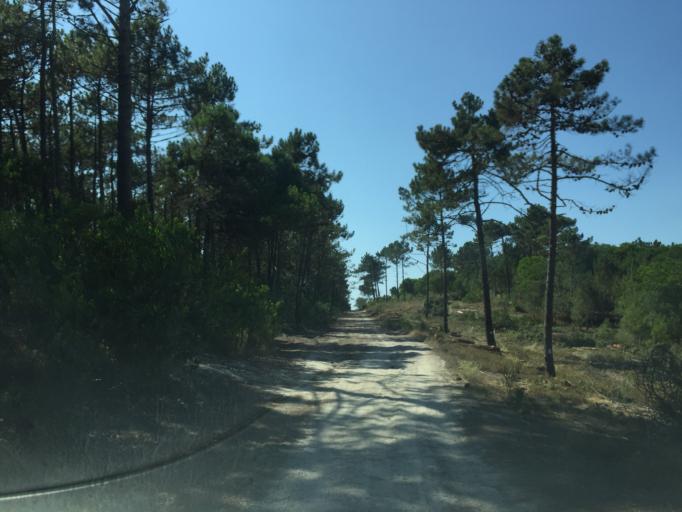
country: PT
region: Coimbra
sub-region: Figueira da Foz
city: Tavarede
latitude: 40.2622
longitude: -8.8583
